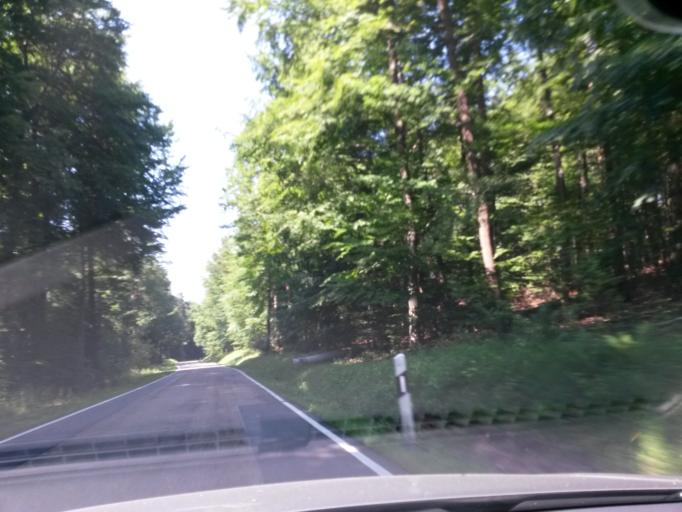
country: DE
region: Baden-Wuerttemberg
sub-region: Karlsruhe Region
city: Neuenburg
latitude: 48.8613
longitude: 8.6043
